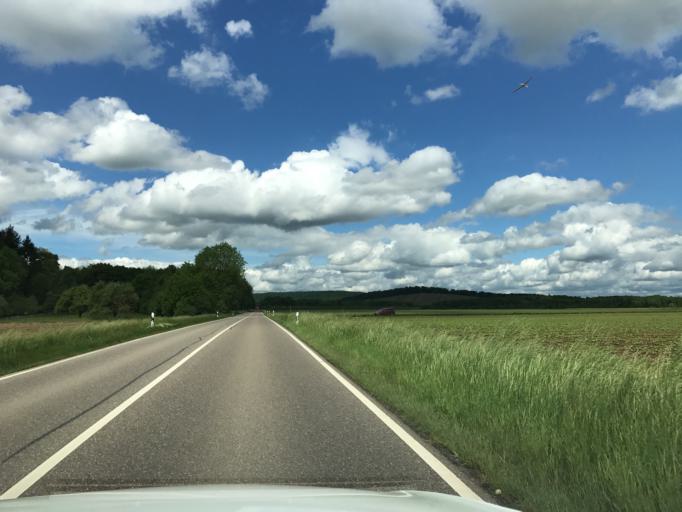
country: DE
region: Baden-Wuerttemberg
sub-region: Regierungsbezirk Stuttgart
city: Lochgau
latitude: 48.9920
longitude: 9.0900
